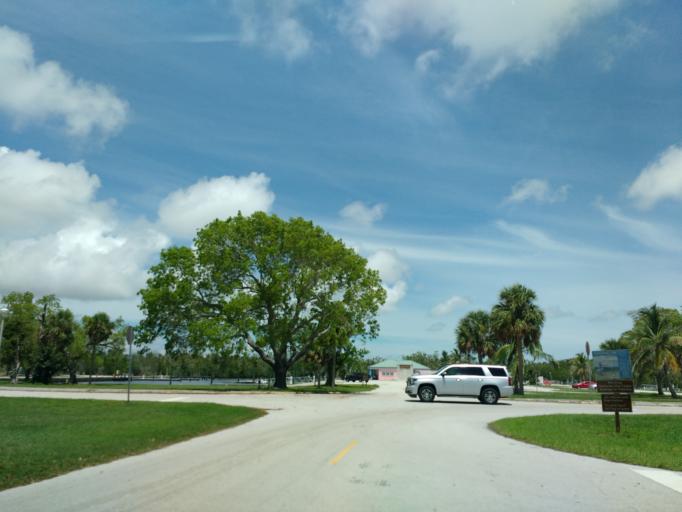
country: US
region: Florida
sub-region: Monroe County
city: Islamorada
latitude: 25.1429
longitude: -80.9243
